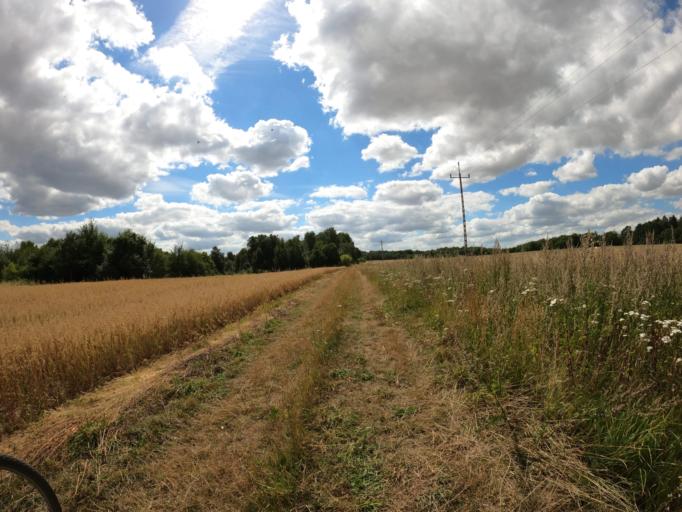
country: PL
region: West Pomeranian Voivodeship
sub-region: Powiat swidwinski
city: Swidwin
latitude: 53.7506
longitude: 15.8270
